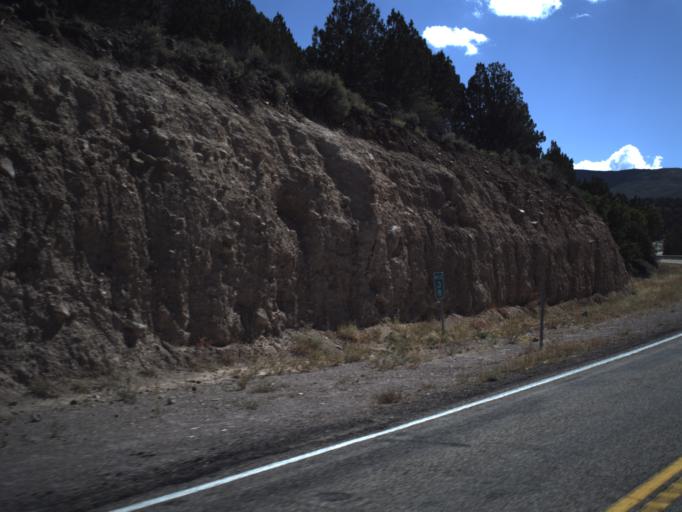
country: US
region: Utah
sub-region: Washington County
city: Enterprise
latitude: 37.5457
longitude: -113.6852
